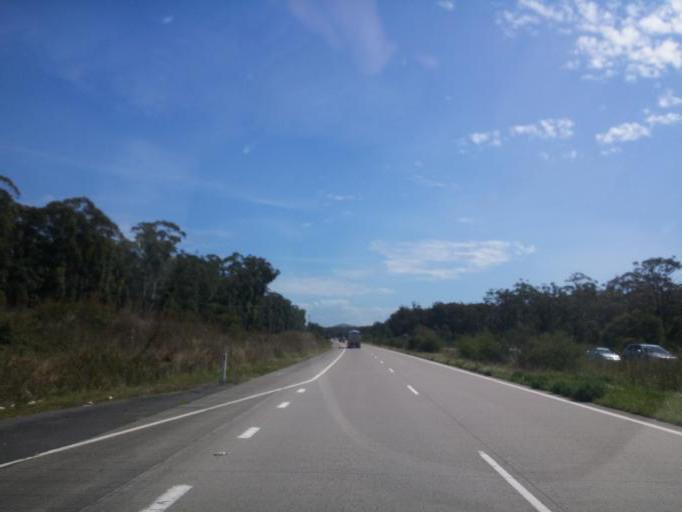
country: AU
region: New South Wales
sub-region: Great Lakes
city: Bulahdelah
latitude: -32.4934
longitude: 152.2025
